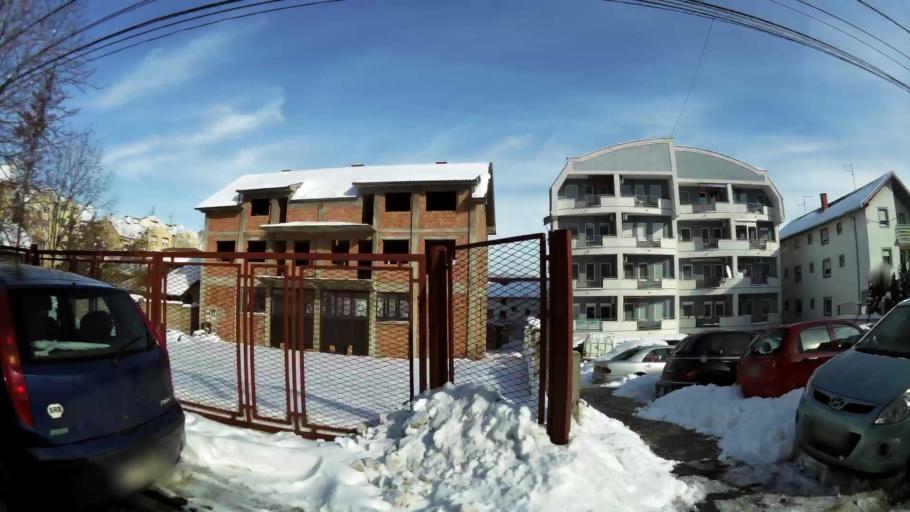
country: RS
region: Central Serbia
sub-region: Belgrade
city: Palilula
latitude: 44.8012
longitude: 20.5239
